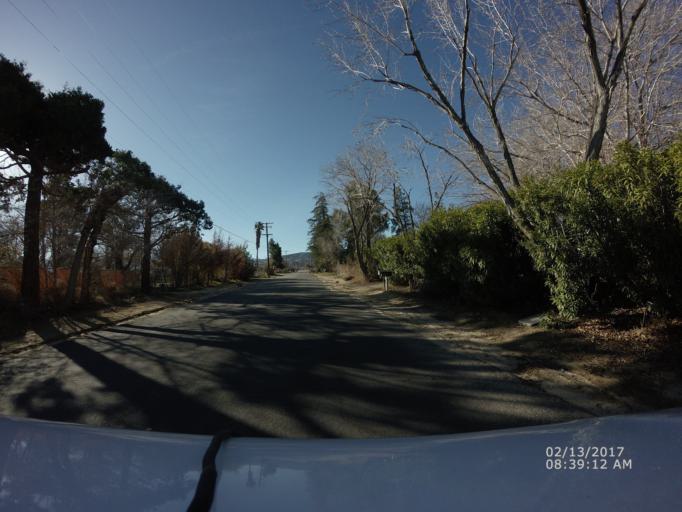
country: US
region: California
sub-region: Los Angeles County
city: Littlerock
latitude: 34.5251
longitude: -117.9881
